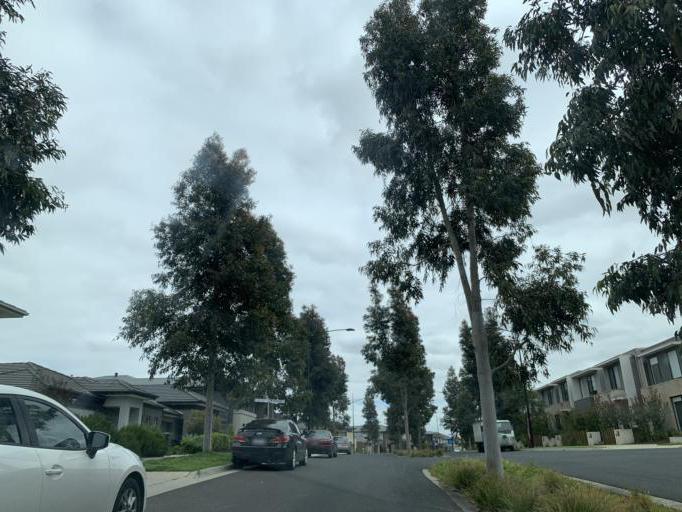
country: AU
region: Victoria
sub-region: Moreland
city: Fawkner
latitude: -37.7301
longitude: 144.9825
